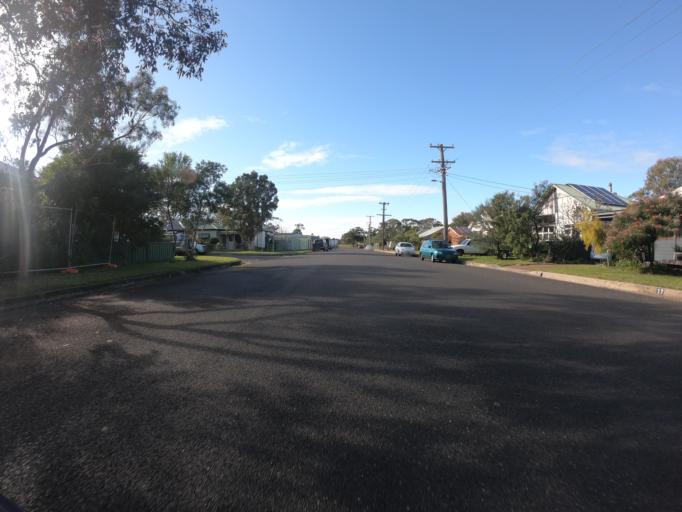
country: AU
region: New South Wales
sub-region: Wollongong
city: East Corrimal
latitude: -34.3674
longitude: 150.9152
